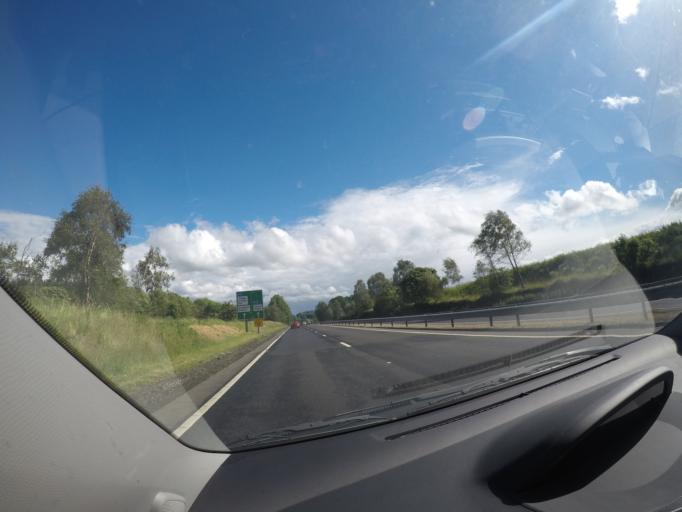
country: GB
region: Scotland
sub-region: Stirling
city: Dunblane
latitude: 56.1773
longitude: -3.9774
